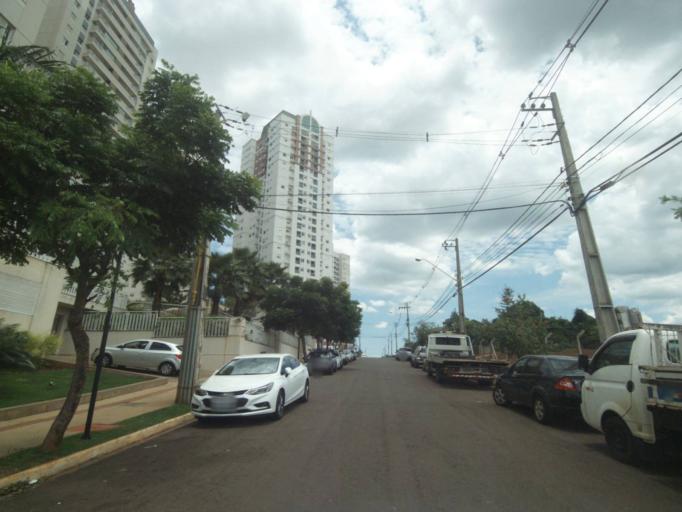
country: BR
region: Parana
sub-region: Londrina
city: Londrina
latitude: -23.3319
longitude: -51.1836
